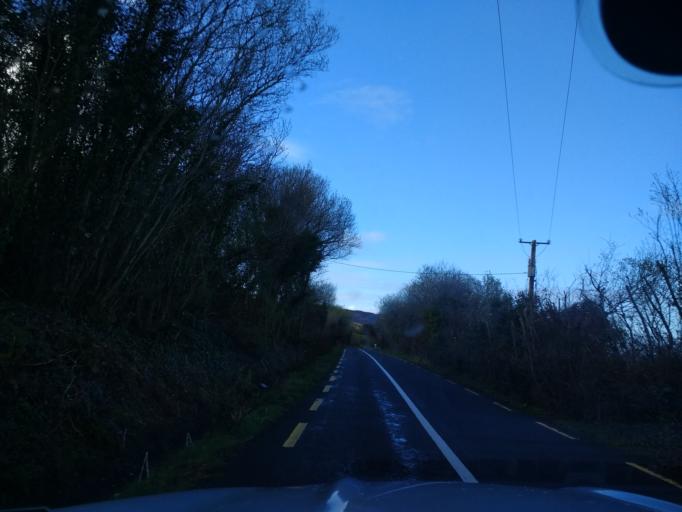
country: IE
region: Ulster
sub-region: County Donegal
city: Buncrana
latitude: 55.1583
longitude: -7.5639
